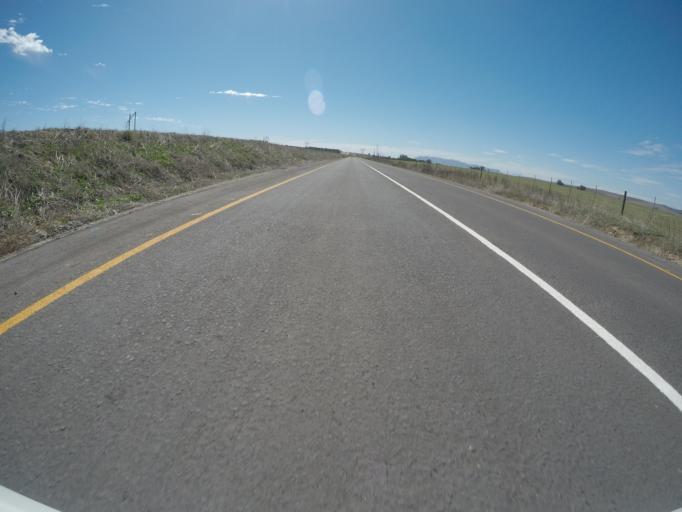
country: ZA
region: Western Cape
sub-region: West Coast District Municipality
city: Malmesbury
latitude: -33.5180
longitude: 18.6535
